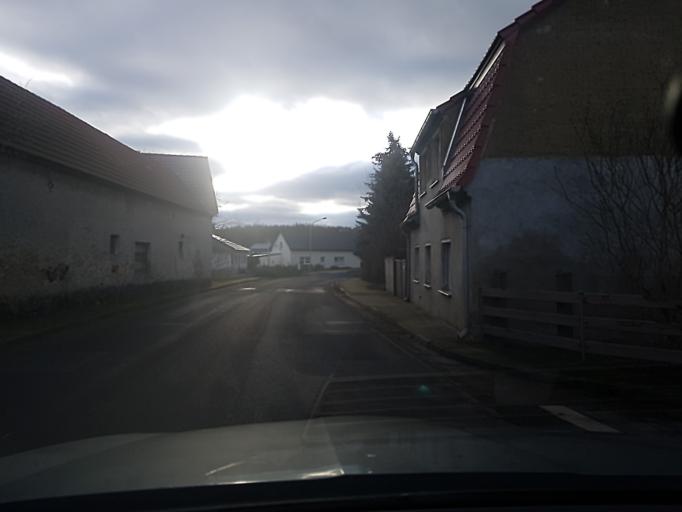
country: DE
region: Brandenburg
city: Bad Liebenwerda
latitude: 51.5586
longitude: 13.4142
